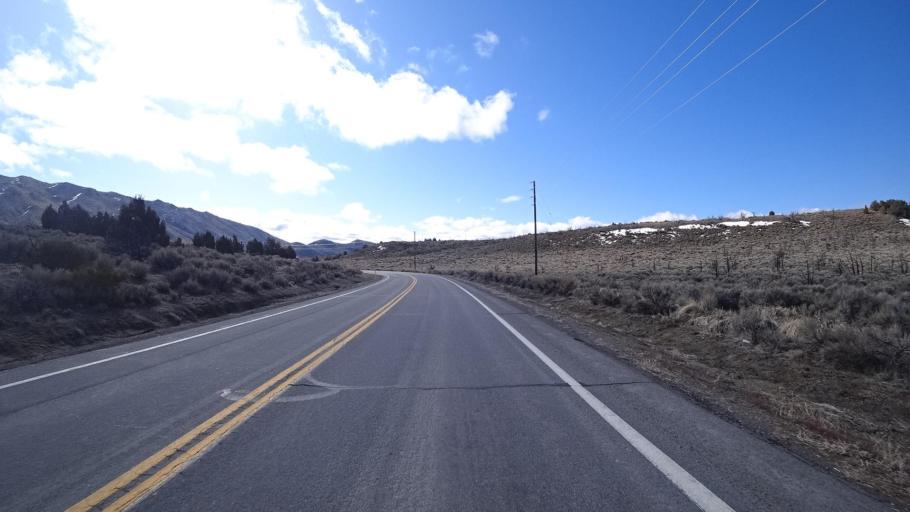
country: US
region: Nevada
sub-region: Washoe County
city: Cold Springs
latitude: 39.7739
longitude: -119.8926
